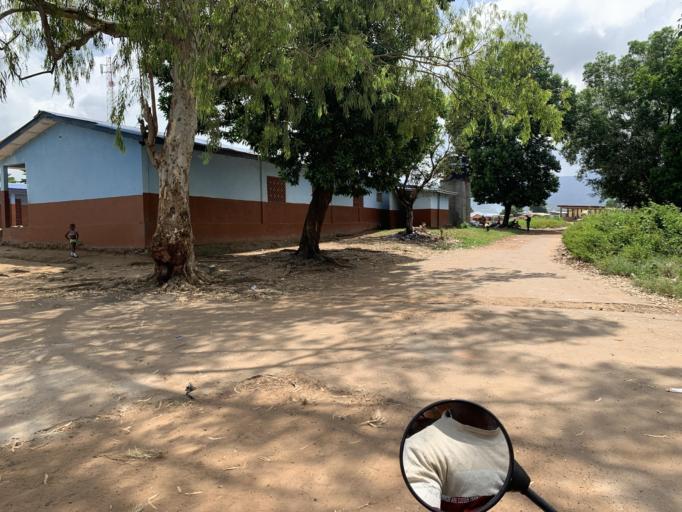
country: SL
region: Western Area
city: Hastings
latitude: 8.4110
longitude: -13.1319
